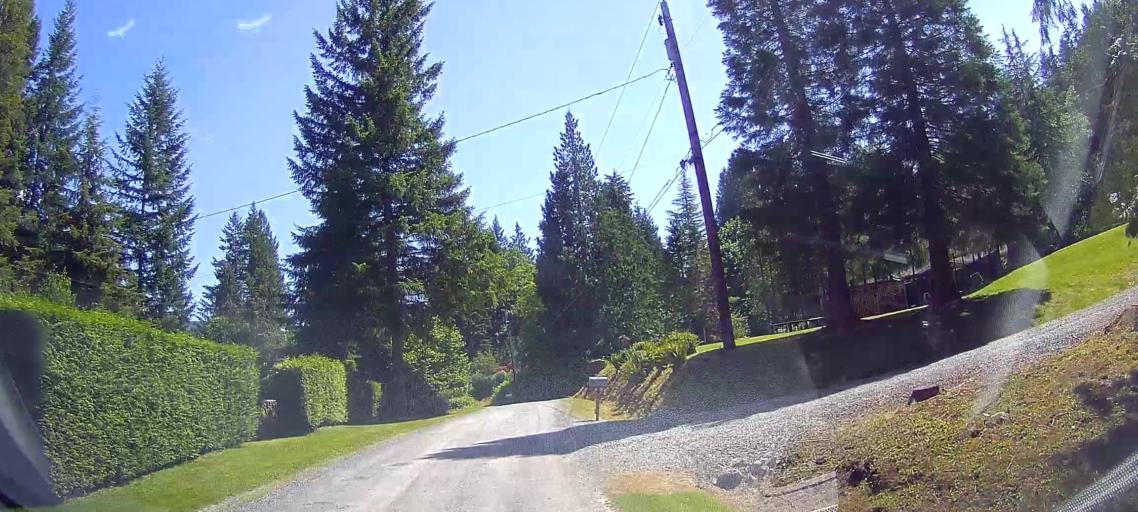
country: US
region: Washington
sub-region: Whatcom County
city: Sudden Valley
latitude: 48.6484
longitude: -122.3318
